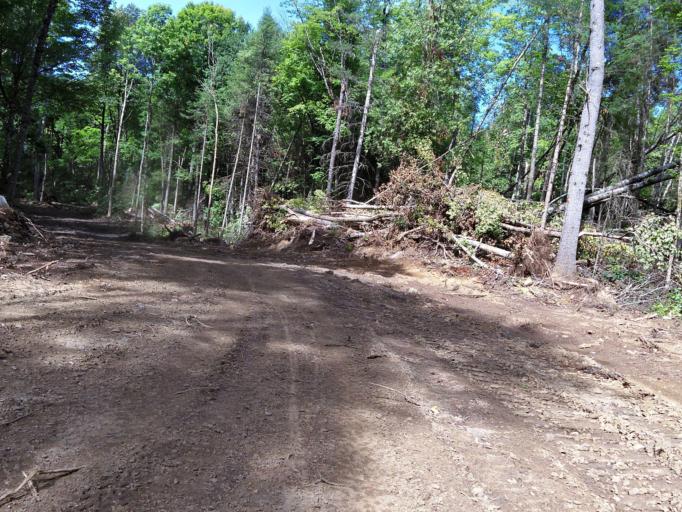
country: CA
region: Ontario
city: Renfrew
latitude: 45.1074
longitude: -76.7178
